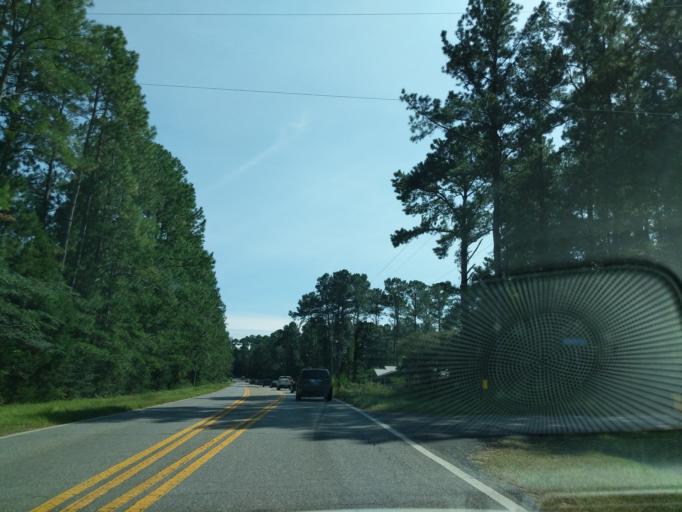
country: US
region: Florida
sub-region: Okaloosa County
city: Crestview
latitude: 30.7343
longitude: -86.6228
